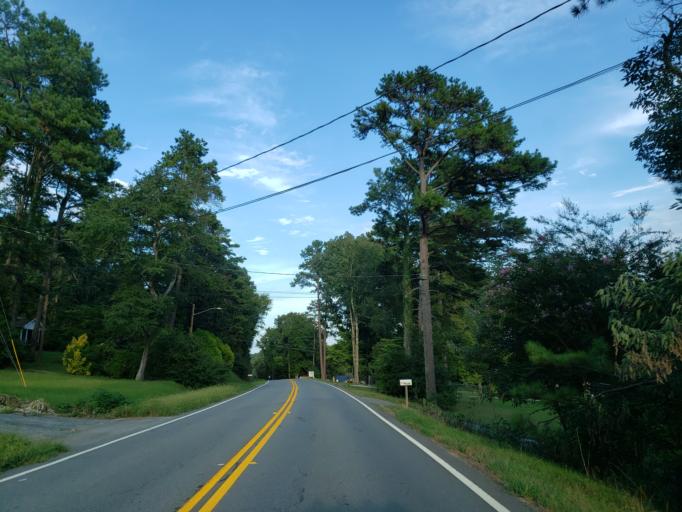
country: US
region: Georgia
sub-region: Bartow County
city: Euharlee
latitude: 34.2376
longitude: -84.9381
